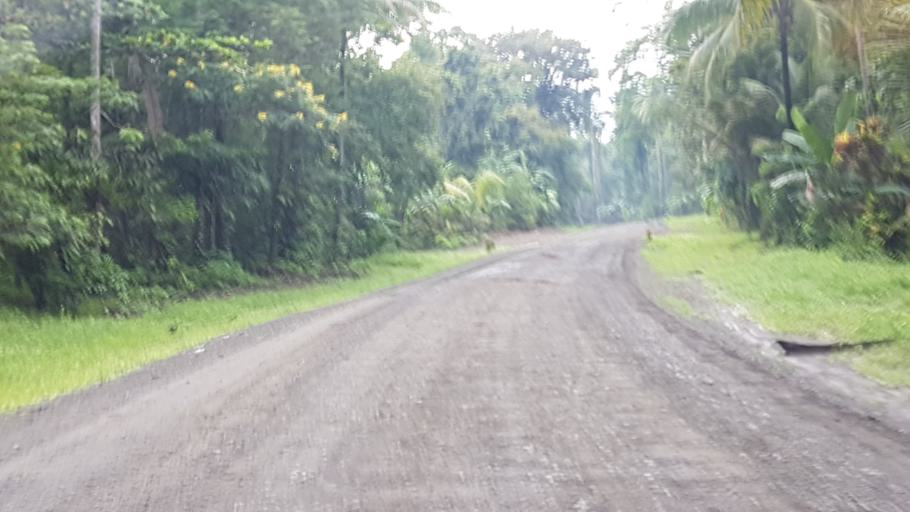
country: PG
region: Milne Bay
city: Alotau
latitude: -10.3289
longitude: 150.5267
